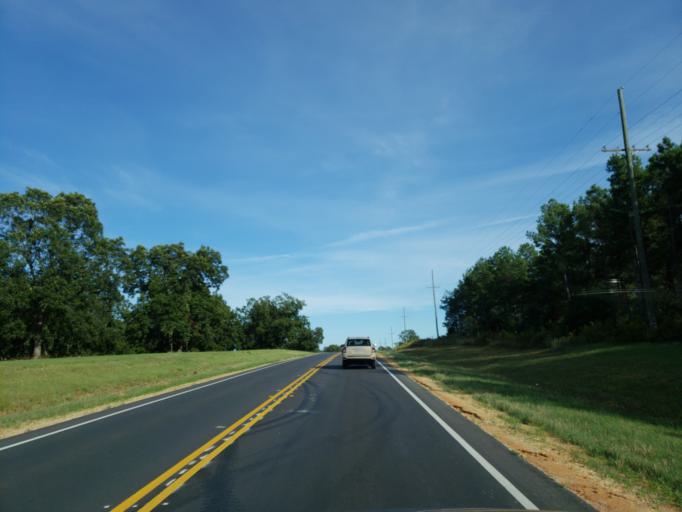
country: US
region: Georgia
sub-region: Houston County
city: Perry
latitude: 32.4846
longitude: -83.7763
